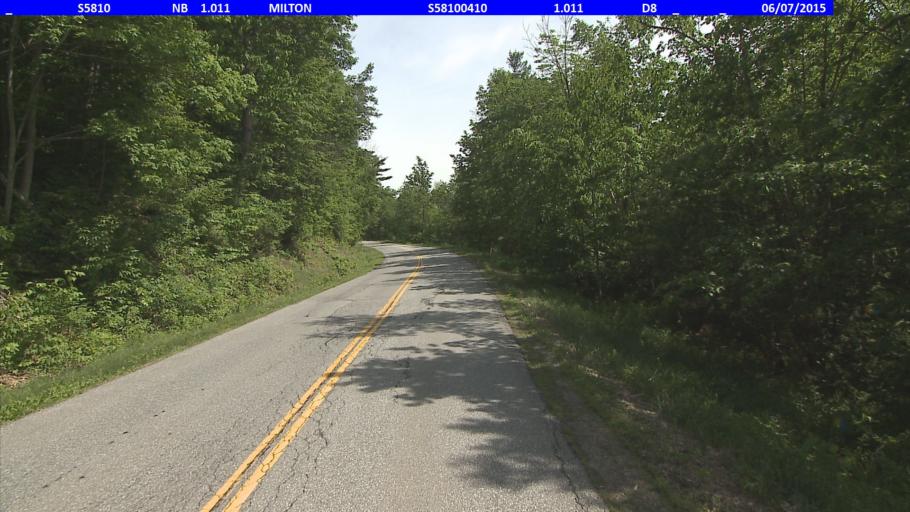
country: US
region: Vermont
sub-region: Chittenden County
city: Milton
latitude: 44.5960
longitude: -73.1287
